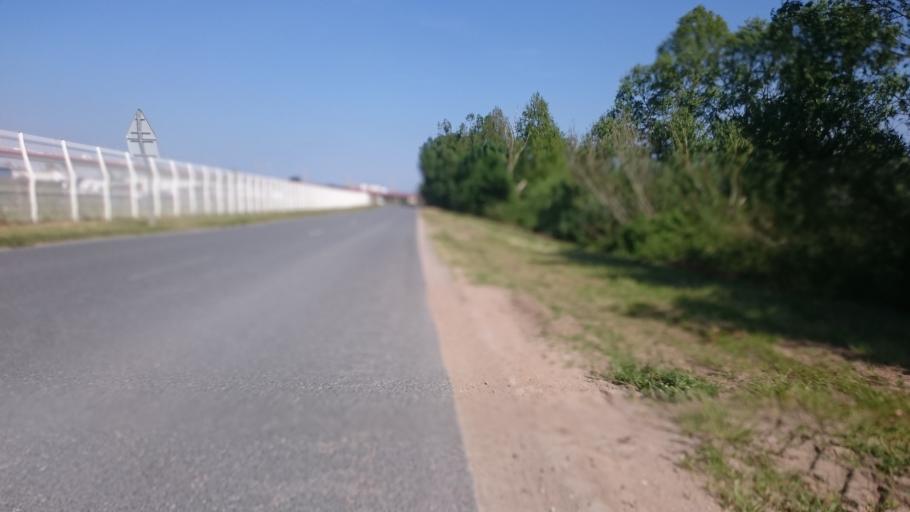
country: FR
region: Pays de la Loire
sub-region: Departement de la Loire-Atlantique
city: Bouguenais
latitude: 47.1848
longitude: -1.6205
